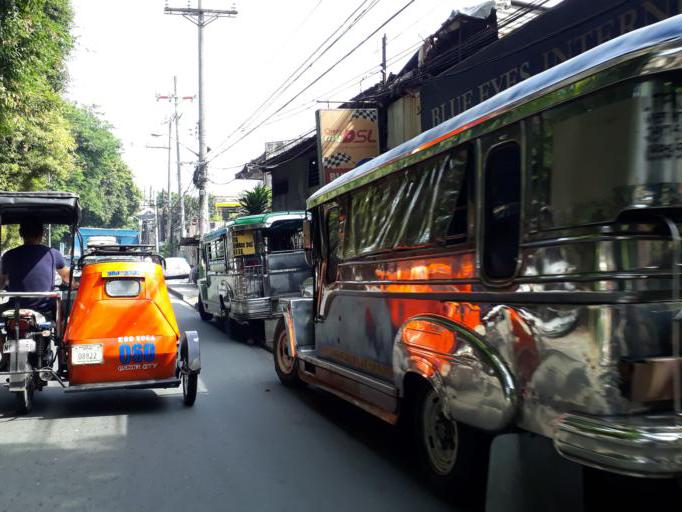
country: PH
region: Calabarzon
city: Bagong Pagasa
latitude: 14.6703
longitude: 121.0061
